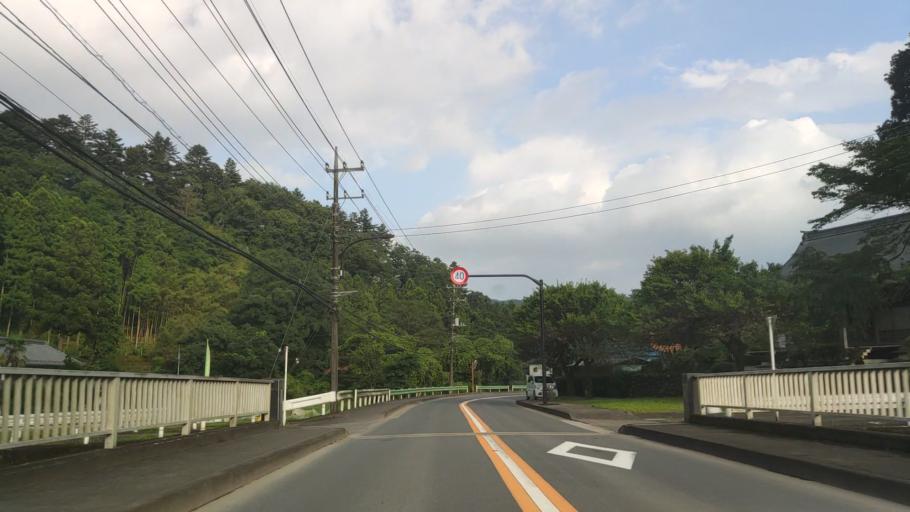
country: JP
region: Tokyo
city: Ome
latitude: 35.8275
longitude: 139.2431
